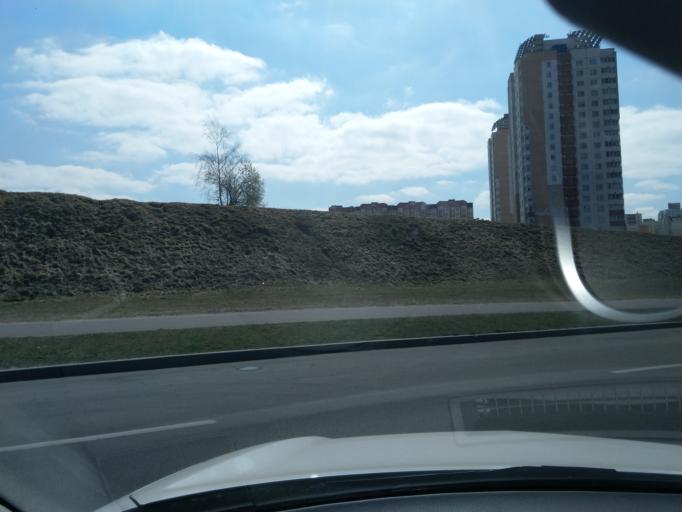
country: BY
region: Minsk
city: Yubilyeyny
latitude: 53.8517
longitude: 27.4888
